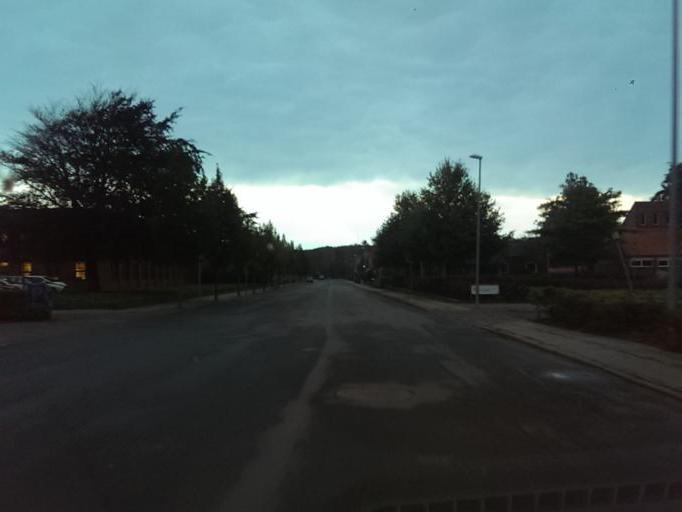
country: DK
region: South Denmark
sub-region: Esbjerg Kommune
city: Bramming
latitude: 55.4652
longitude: 8.7024
